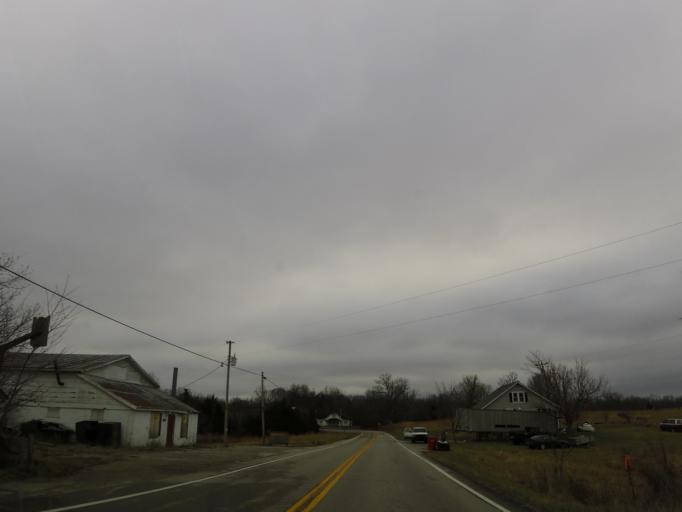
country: US
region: Kentucky
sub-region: Franklin County
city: Frankfort
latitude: 38.3418
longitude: -84.9635
